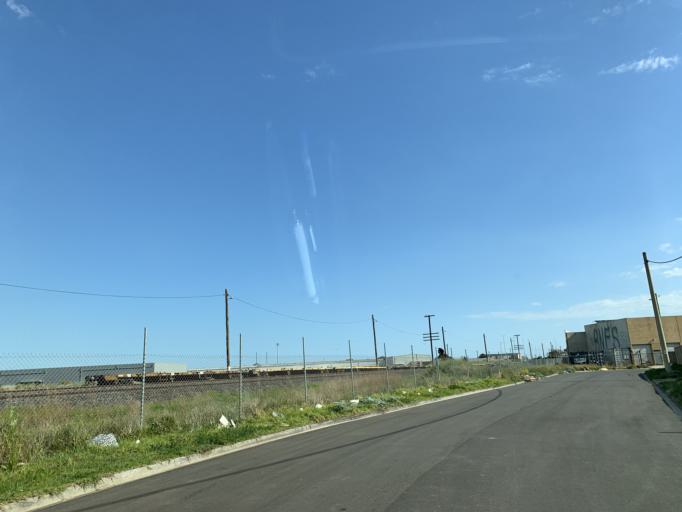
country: AU
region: Victoria
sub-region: Brimbank
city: Albion
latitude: -37.7559
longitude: 144.8379
